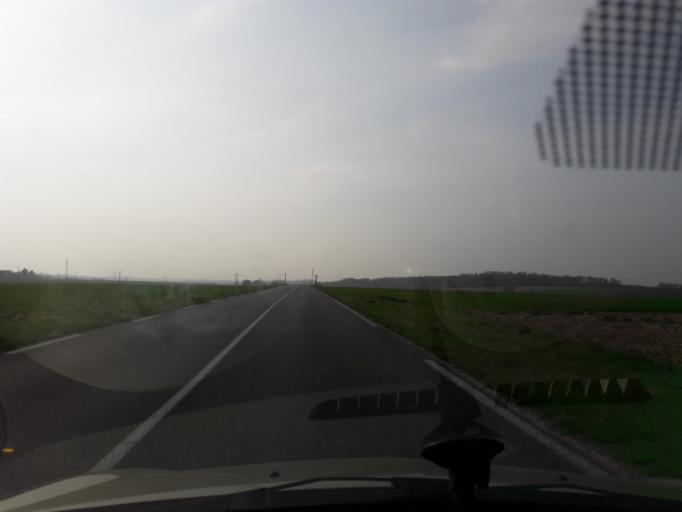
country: FR
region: Nord-Pas-de-Calais
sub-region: Departement du Nord
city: Recquignies
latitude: 50.2561
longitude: 4.0580
